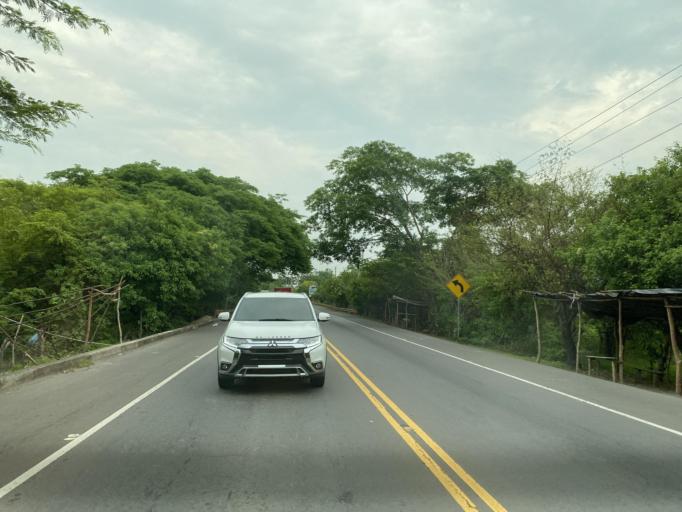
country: SV
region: San Miguel
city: Chirilagua
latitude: 13.3283
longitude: -88.1576
